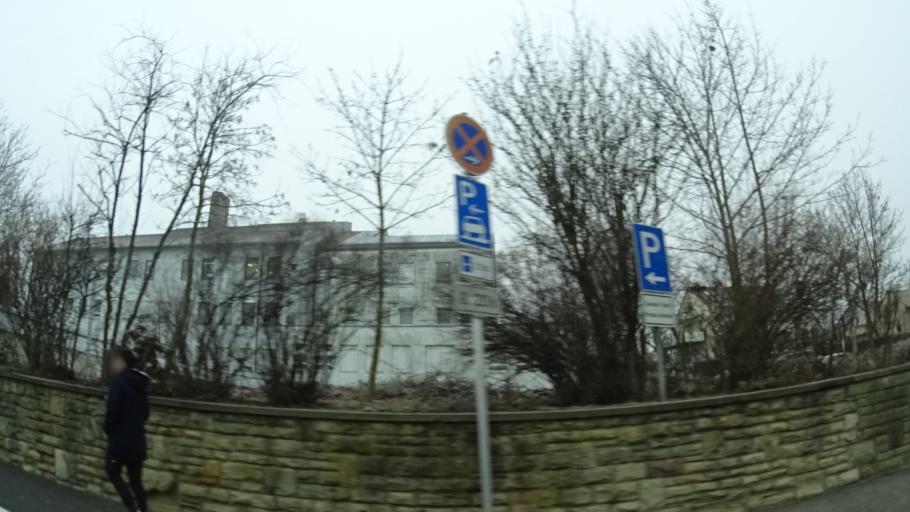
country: DE
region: Bavaria
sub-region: Regierungsbezirk Unterfranken
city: Gerolzhofen
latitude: 49.8996
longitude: 10.3561
